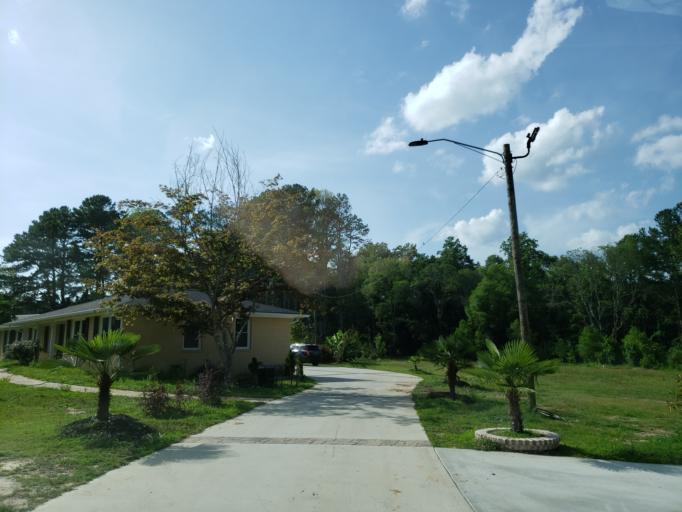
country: US
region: Georgia
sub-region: Cobb County
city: Austell
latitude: 33.8699
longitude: -84.6170
